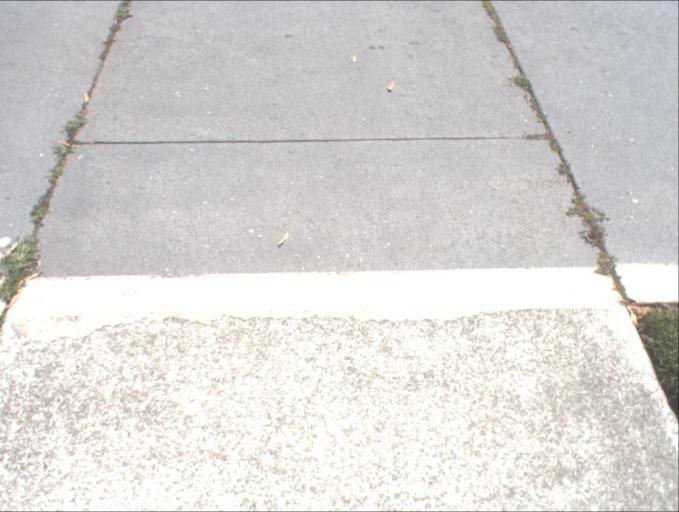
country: AU
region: Queensland
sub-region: Logan
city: Windaroo
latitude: -27.7517
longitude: 153.1850
